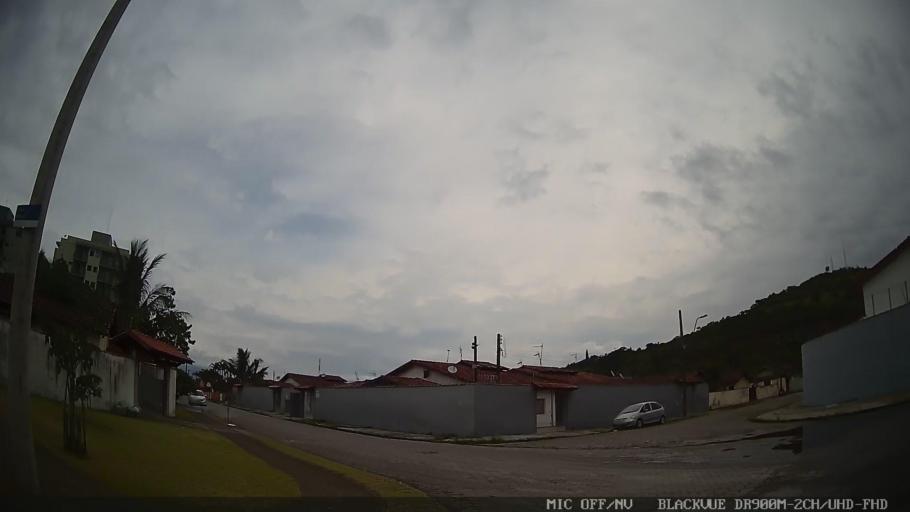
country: BR
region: Sao Paulo
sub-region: Caraguatatuba
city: Caraguatatuba
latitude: -23.6181
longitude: -45.3891
